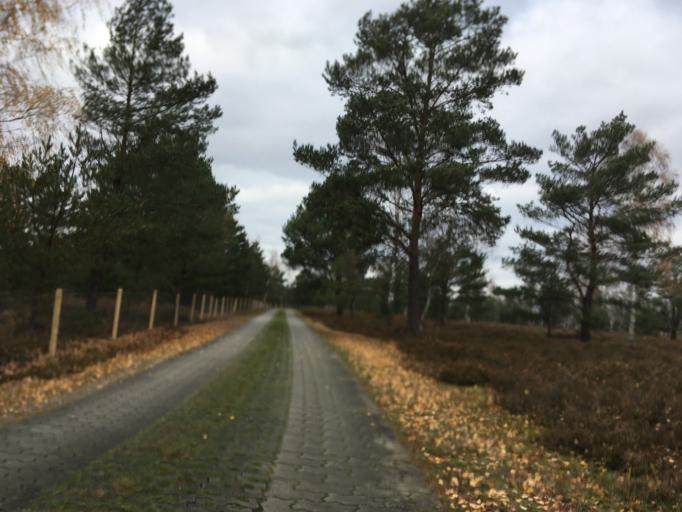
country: DE
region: Brandenburg
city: Tauer
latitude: 52.0068
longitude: 14.4991
